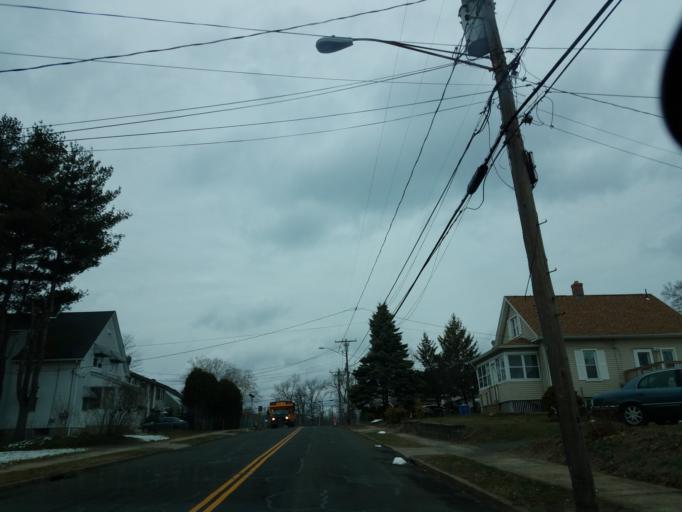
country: US
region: Connecticut
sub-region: Hartford County
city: New Britain
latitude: 41.6897
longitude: -72.7971
